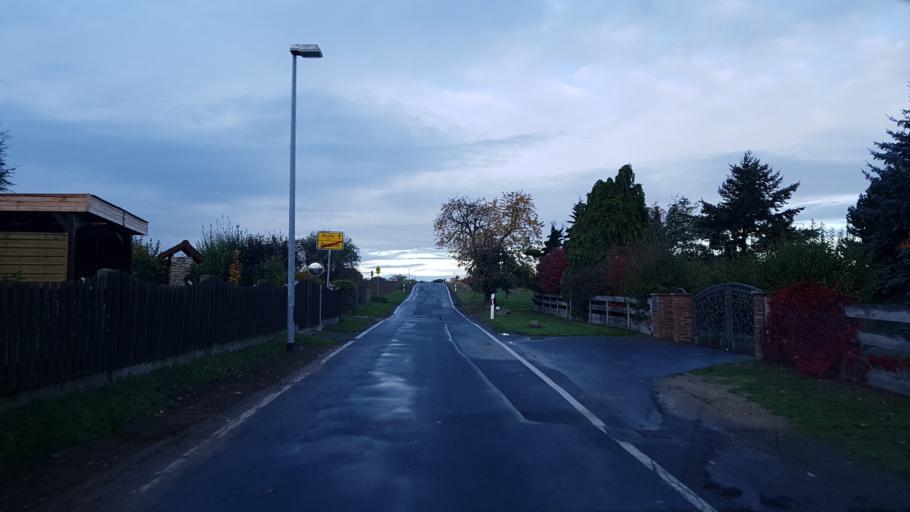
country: DE
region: Saxony
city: Dahlen
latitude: 51.3887
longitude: 13.0575
